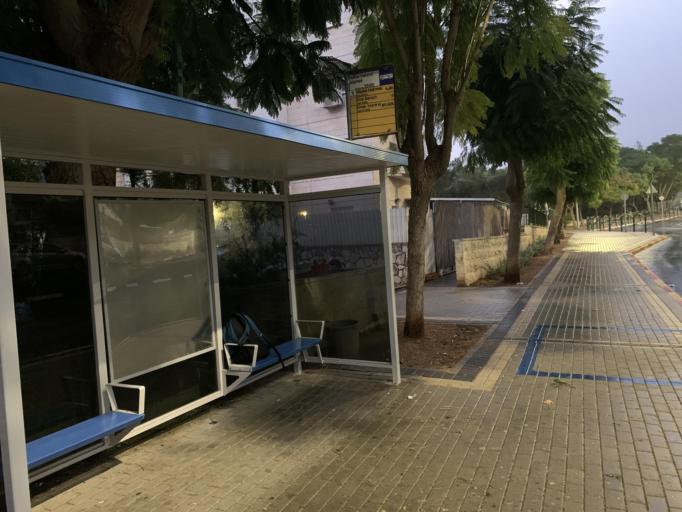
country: IL
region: Northern District
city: Migdal Ha`Emeq
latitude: 32.6826
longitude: 35.2447
